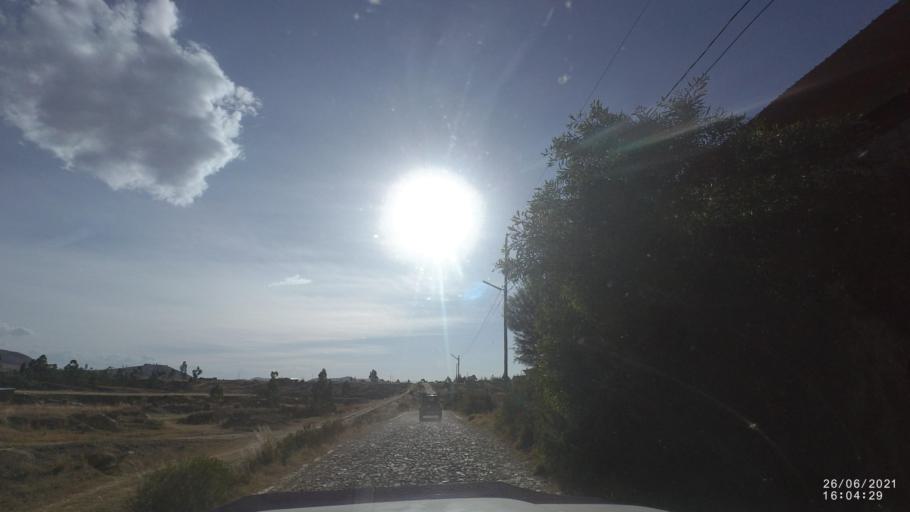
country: BO
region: Cochabamba
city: Arani
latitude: -17.8319
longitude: -65.7569
